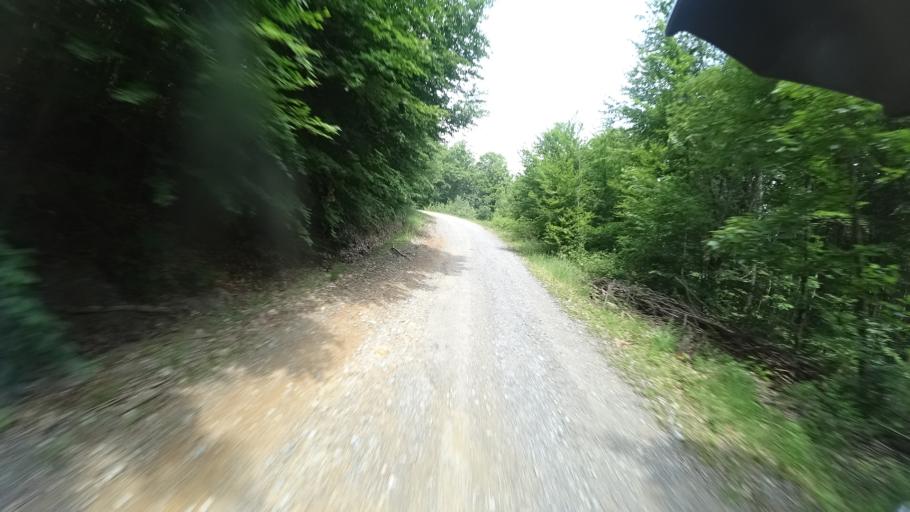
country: HR
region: Sisacko-Moslavacka
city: Gvozd
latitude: 45.3187
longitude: 15.8130
